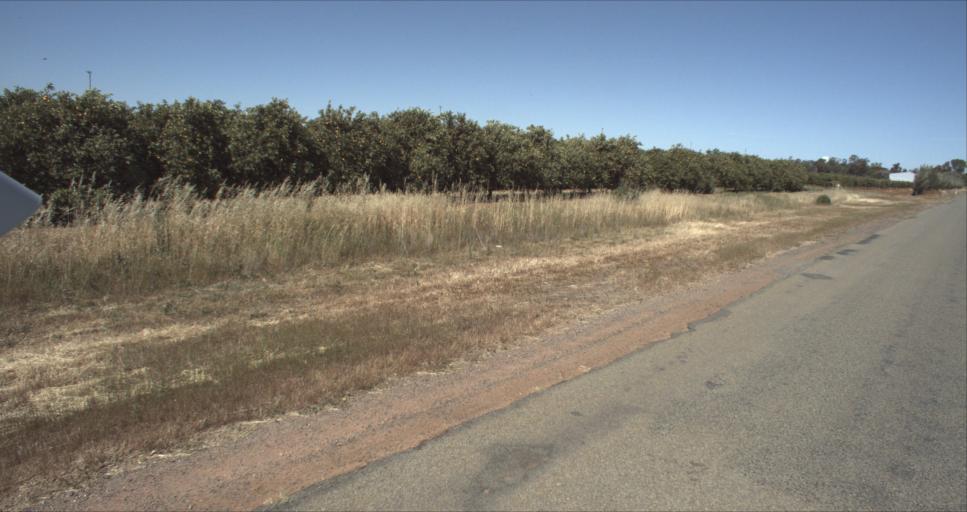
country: AU
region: New South Wales
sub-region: Leeton
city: Leeton
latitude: -34.5441
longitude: 146.3665
